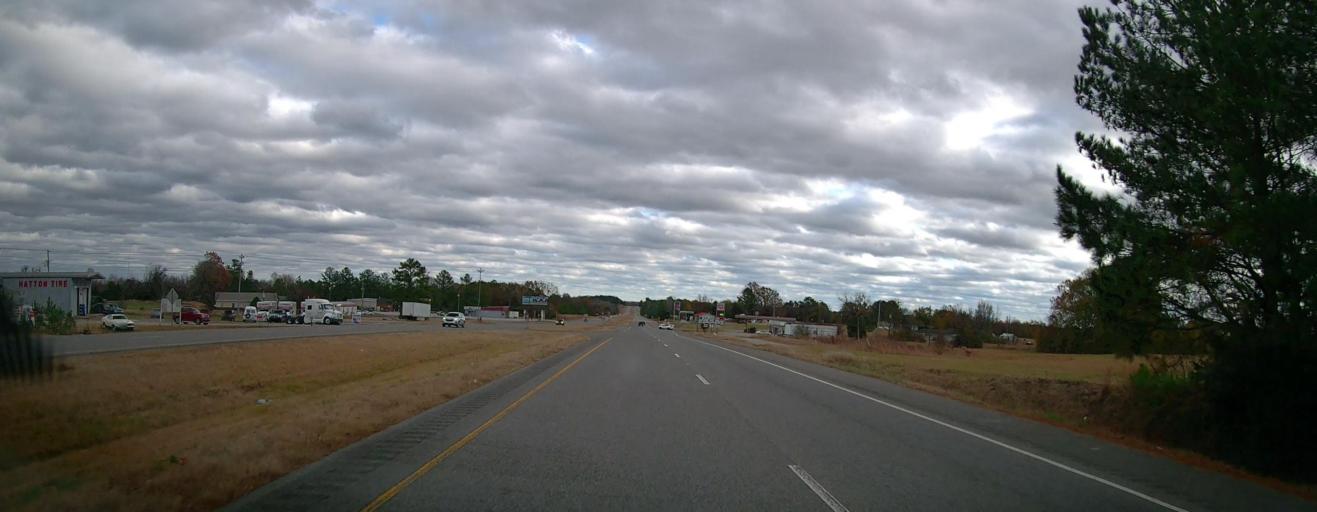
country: US
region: Alabama
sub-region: Lawrence County
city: Town Creek
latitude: 34.5907
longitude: -87.4272
